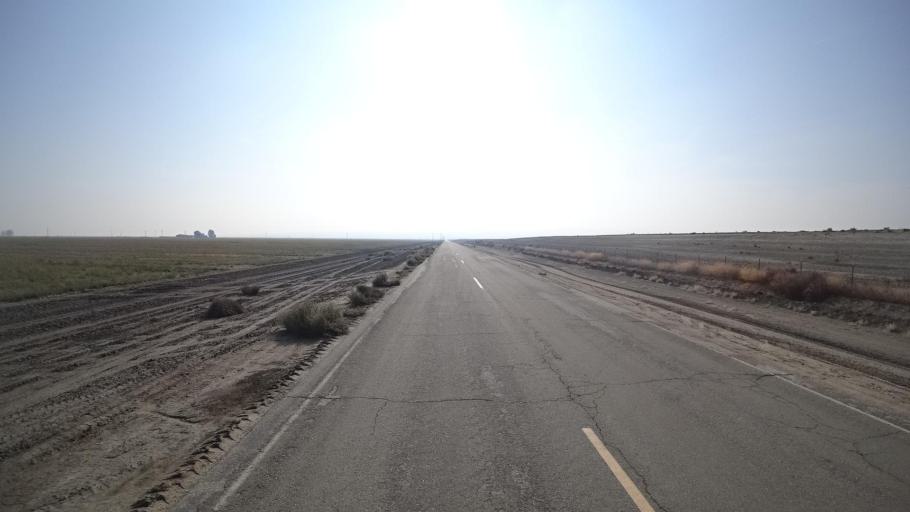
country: US
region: California
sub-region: Kern County
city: Buttonwillow
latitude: 35.3374
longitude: -119.3767
